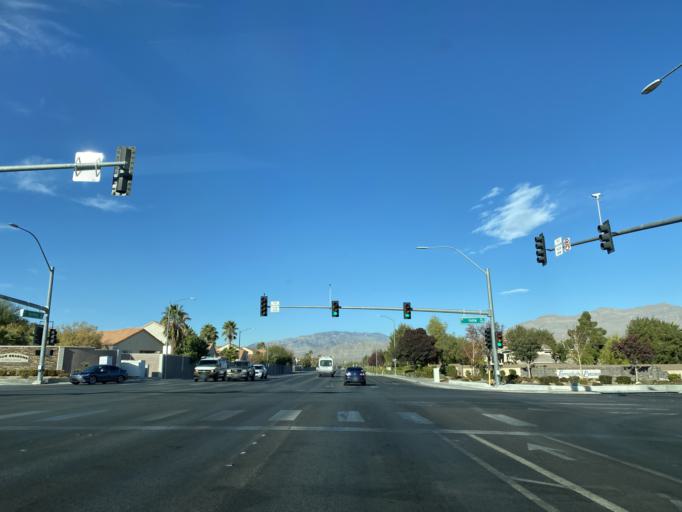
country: US
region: Nevada
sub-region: Clark County
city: North Las Vegas
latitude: 36.2975
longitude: -115.2601
